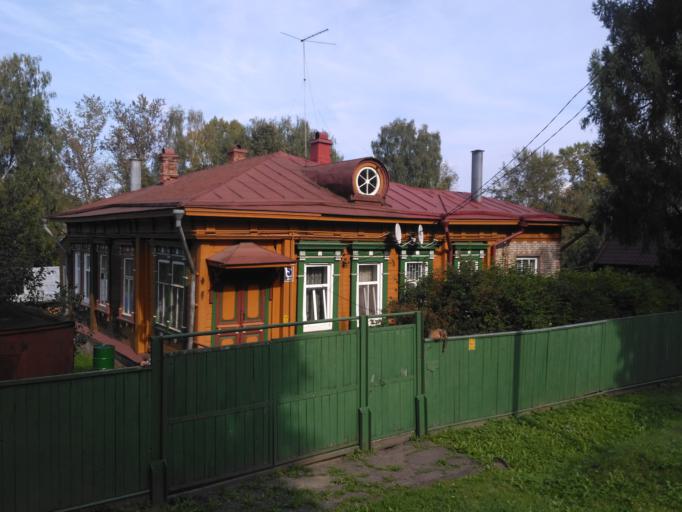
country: RU
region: Moskovskaya
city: Sergiyev Posad
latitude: 56.3106
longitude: 38.1531
